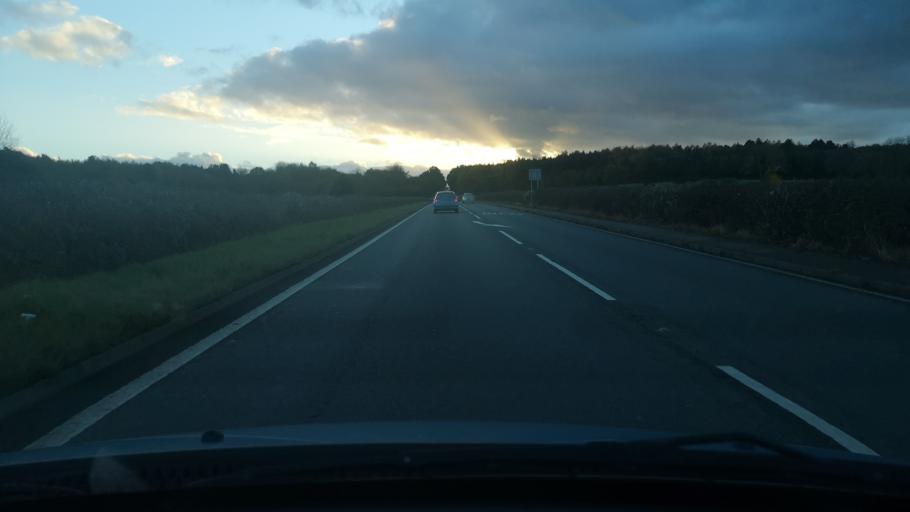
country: GB
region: England
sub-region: City and Borough of Wakefield
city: Crigglestone
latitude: 53.6371
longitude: -1.5501
